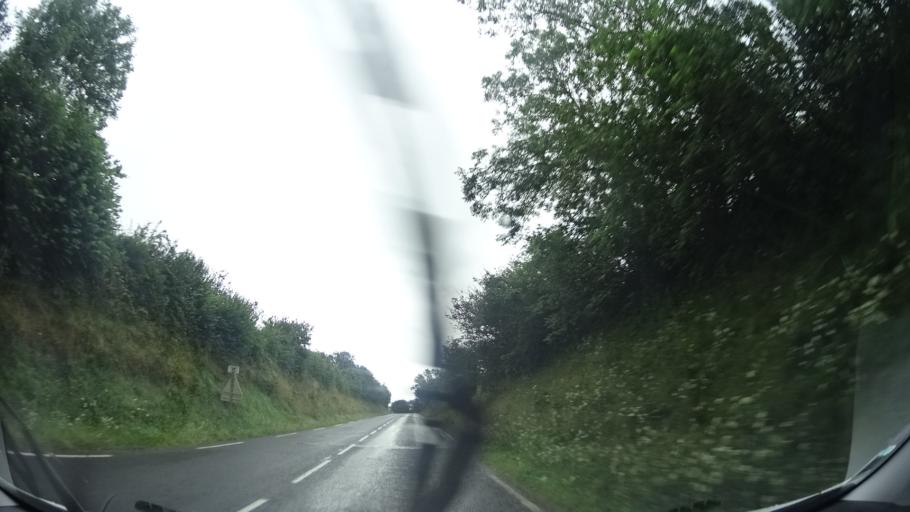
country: FR
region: Lower Normandy
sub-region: Departement de la Manche
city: Beaumont-Hague
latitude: 49.6065
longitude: -1.7889
